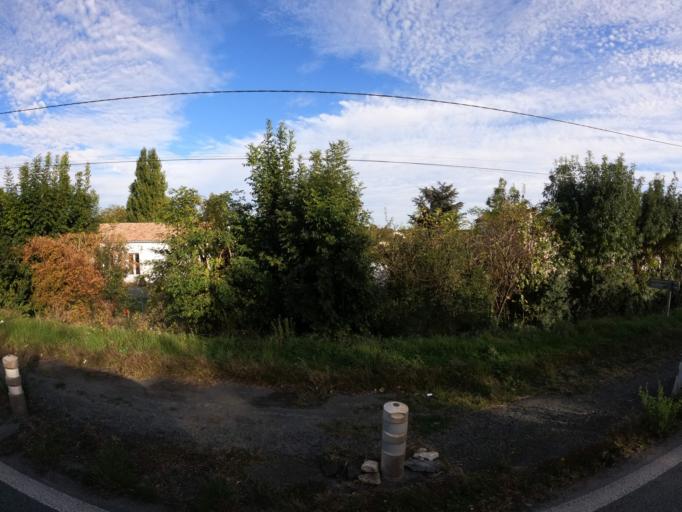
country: FR
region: Poitou-Charentes
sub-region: Departement de la Charente-Maritime
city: Sainte-Soulle
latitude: 46.2059
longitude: -1.0271
